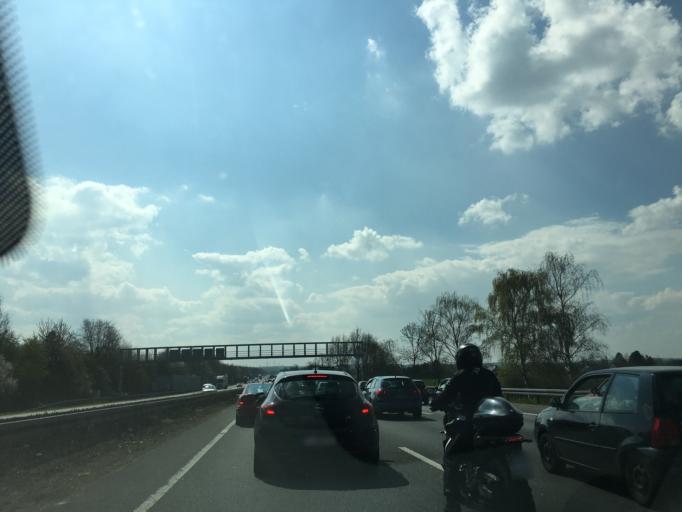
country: DE
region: North Rhine-Westphalia
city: Kamen
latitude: 51.5594
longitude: 7.6646
